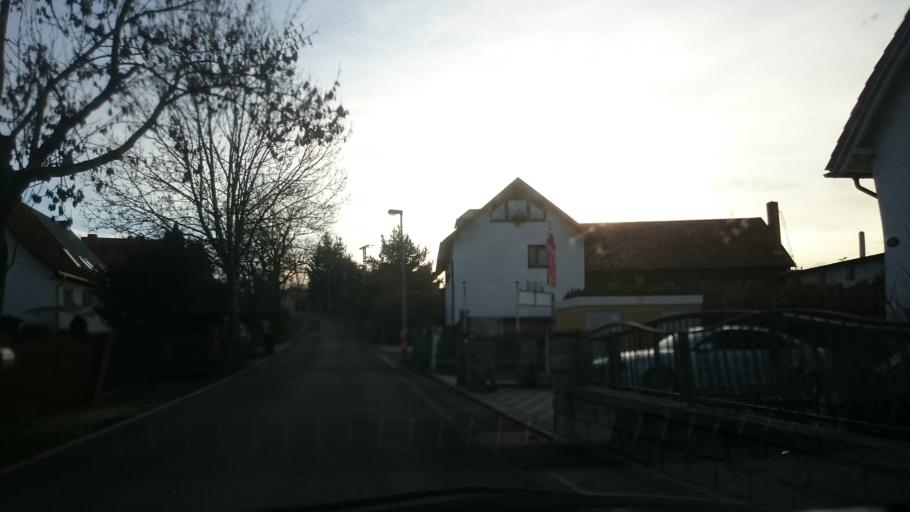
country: DE
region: Saxony
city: Zwickau
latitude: 50.7401
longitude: 12.5177
